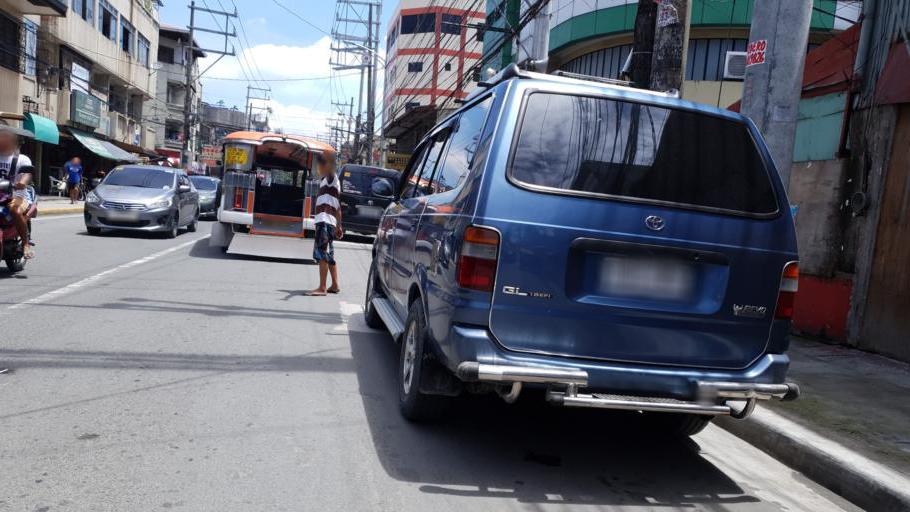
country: PH
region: Metro Manila
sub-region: City of Manila
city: Quiapo
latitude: 14.5740
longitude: 121.0039
